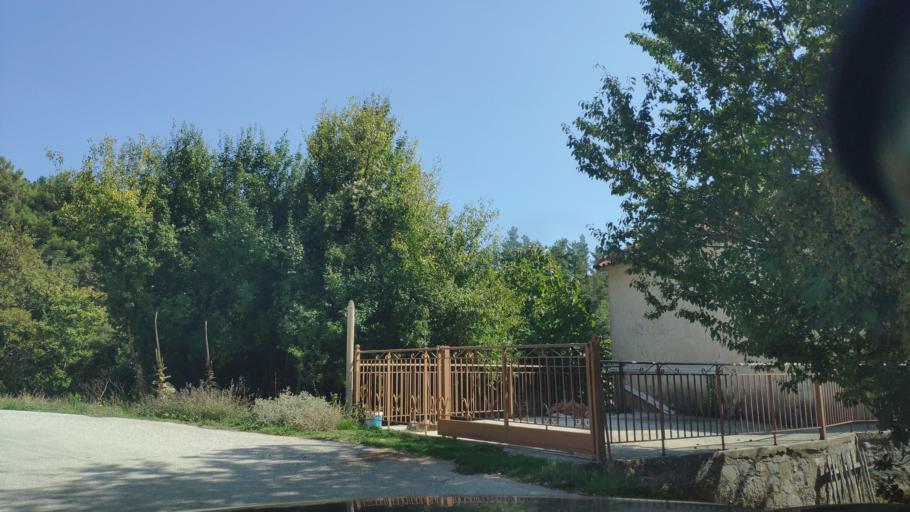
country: GR
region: Peloponnese
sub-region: Nomos Korinthias
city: Nemea
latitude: 37.8647
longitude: 22.3851
